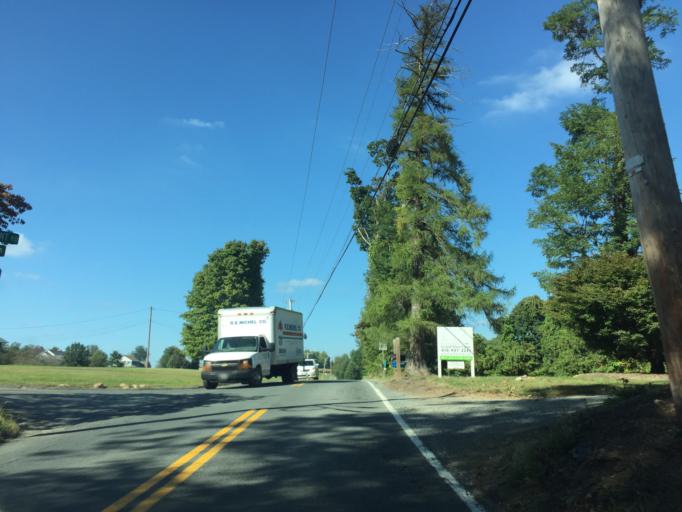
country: US
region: Maryland
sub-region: Harford County
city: Bel Air North
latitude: 39.5657
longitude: -76.4241
